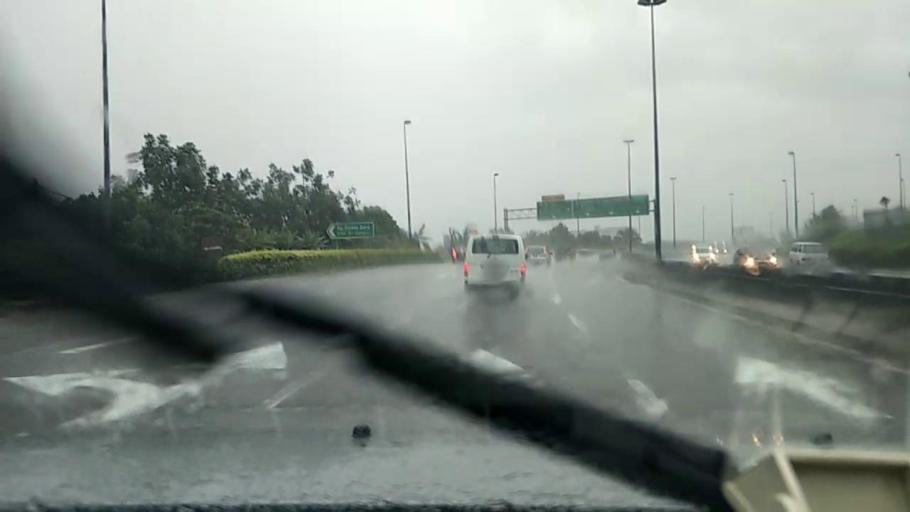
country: MY
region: Selangor
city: Kampong Baharu Balakong
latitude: 2.9888
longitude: 101.7681
